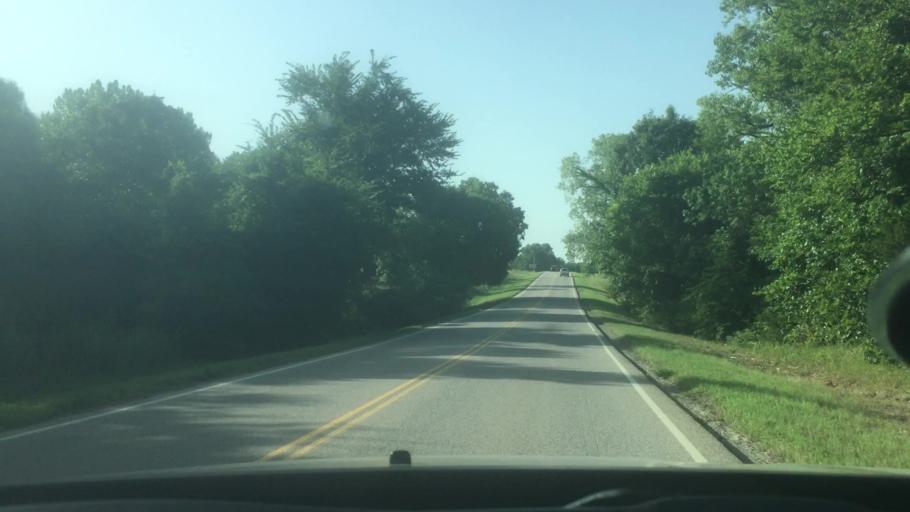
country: US
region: Oklahoma
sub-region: Bryan County
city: Durant
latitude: 34.1910
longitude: -96.4190
